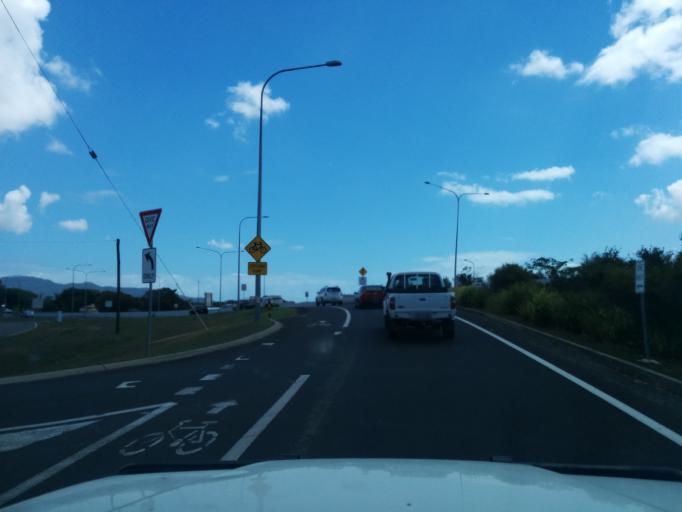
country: AU
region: Queensland
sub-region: Cairns
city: Woree
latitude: -16.9562
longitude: 145.7471
